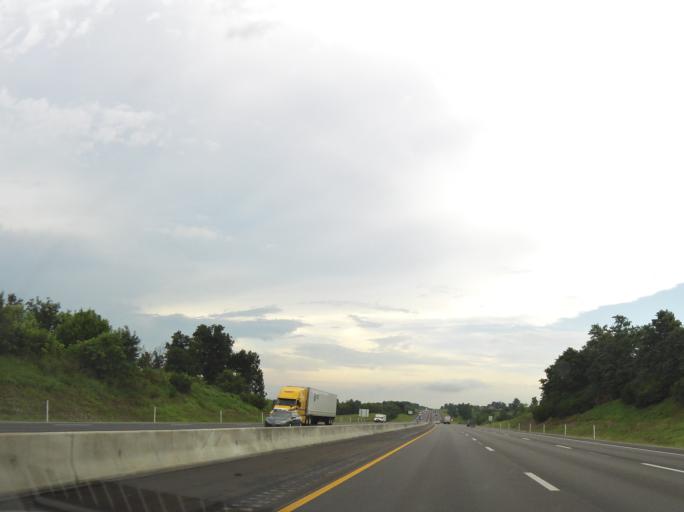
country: US
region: Kentucky
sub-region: Madison County
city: Richmond
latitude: 37.6867
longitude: -84.3141
